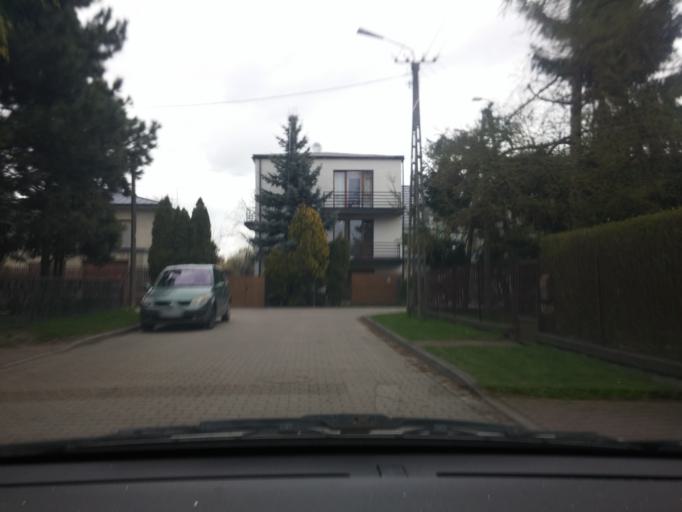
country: PL
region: Masovian Voivodeship
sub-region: Siedlce
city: Siedlce
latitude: 52.1651
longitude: 22.2577
